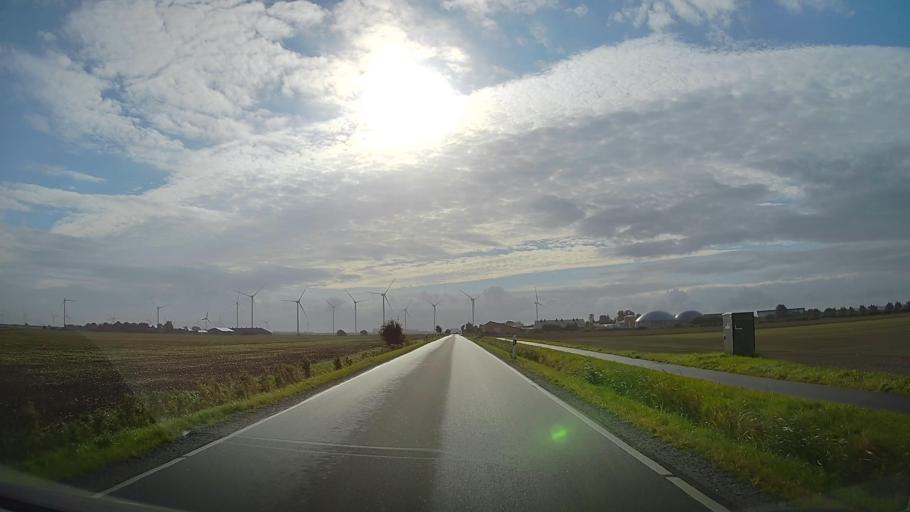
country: DE
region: Schleswig-Holstein
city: Reussenkoge
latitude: 54.5890
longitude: 8.9177
